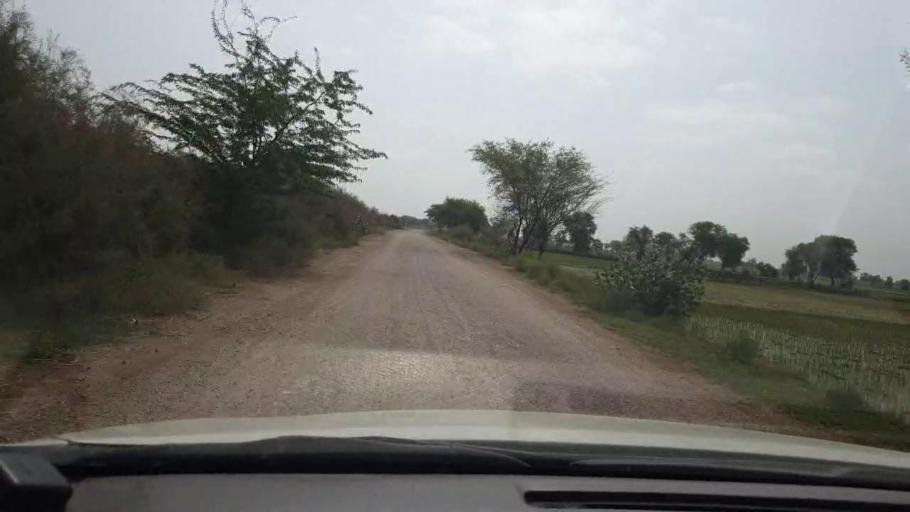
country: PK
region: Sindh
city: Shikarpur
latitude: 28.0069
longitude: 68.5792
